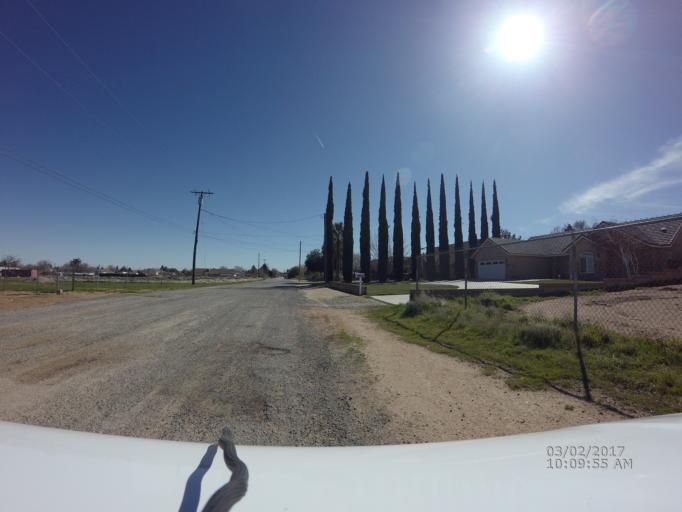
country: US
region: California
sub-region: Los Angeles County
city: Quartz Hill
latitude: 34.6435
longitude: -118.2312
